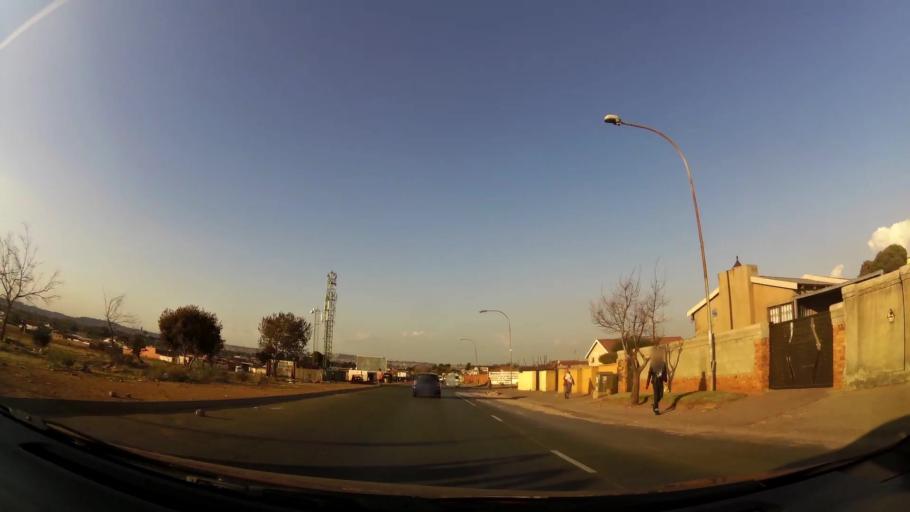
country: ZA
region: Gauteng
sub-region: City of Johannesburg Metropolitan Municipality
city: Soweto
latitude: -26.2271
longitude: 27.8542
